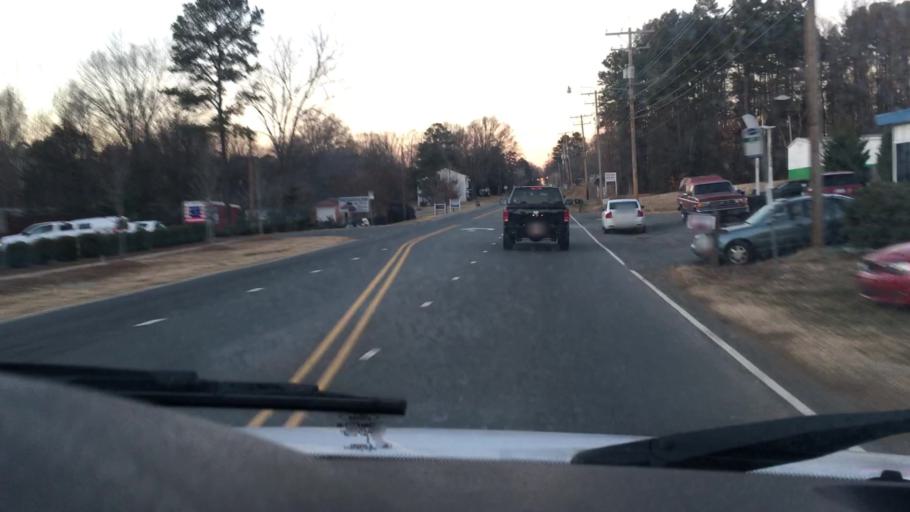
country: US
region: North Carolina
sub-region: Mecklenburg County
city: Huntersville
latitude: 35.4213
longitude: -80.8420
